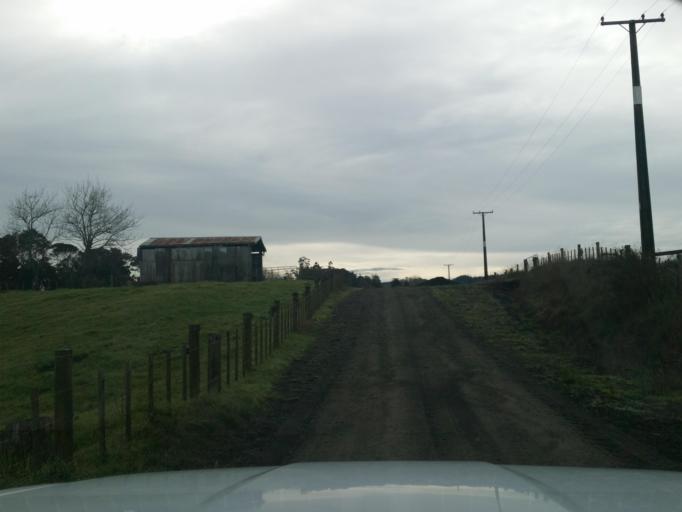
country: NZ
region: Northland
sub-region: Whangarei
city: Maungatapere
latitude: -35.7985
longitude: 174.0541
